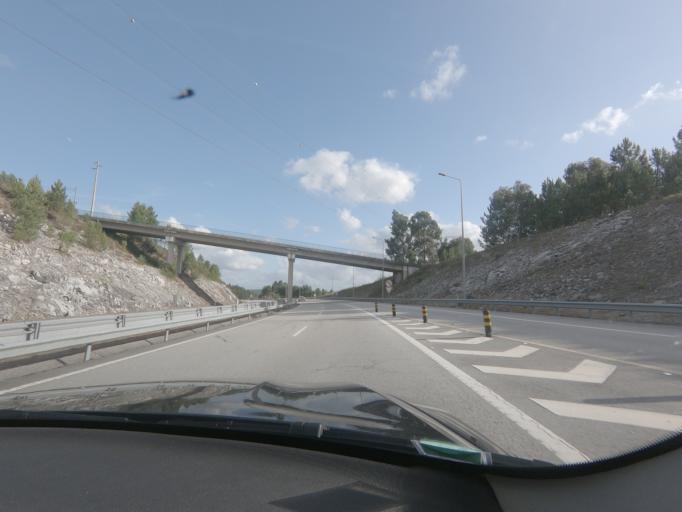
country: PT
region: Viseu
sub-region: Castro Daire
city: Castro Daire
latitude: 40.8186
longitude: -7.9400
